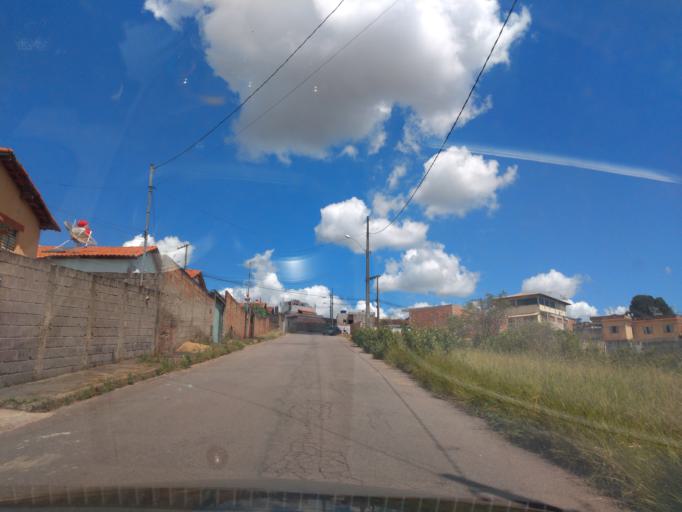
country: BR
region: Minas Gerais
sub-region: Tres Coracoes
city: Tres Coracoes
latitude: -21.6827
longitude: -45.2485
